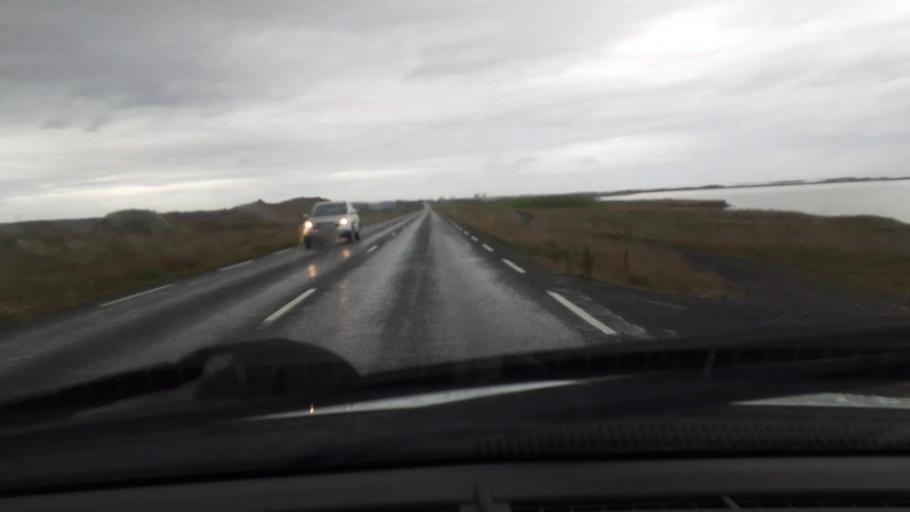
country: IS
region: West
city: Akranes
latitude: 64.3482
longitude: -22.0026
